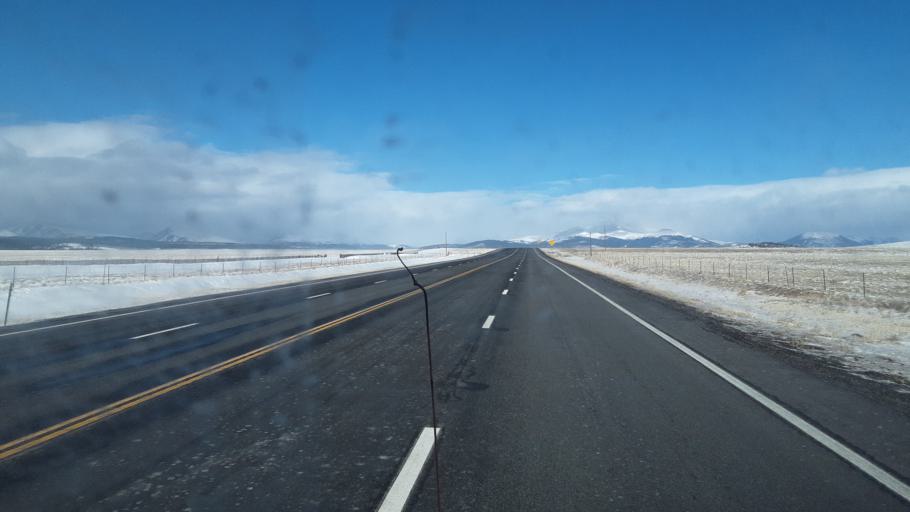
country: US
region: Colorado
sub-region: Park County
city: Fairplay
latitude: 39.1410
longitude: -105.9969
